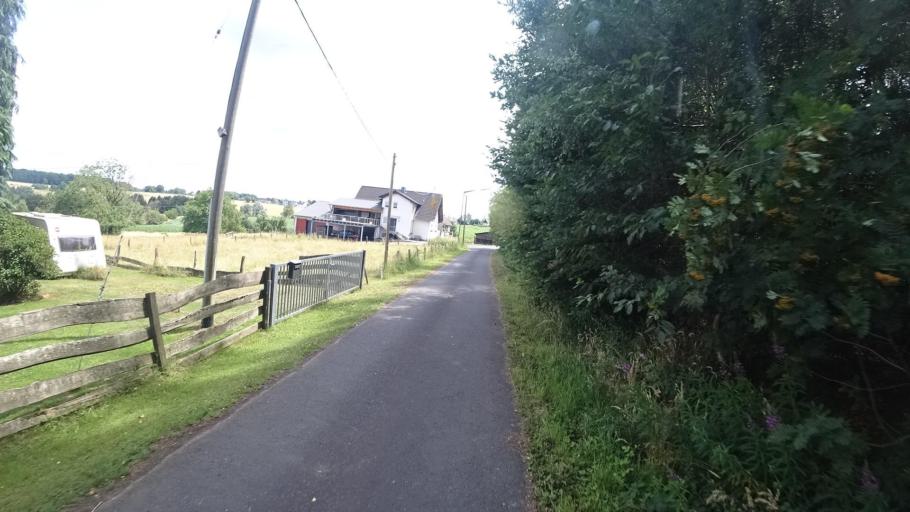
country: DE
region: Rheinland-Pfalz
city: Oberirsen
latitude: 50.7116
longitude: 7.5748
